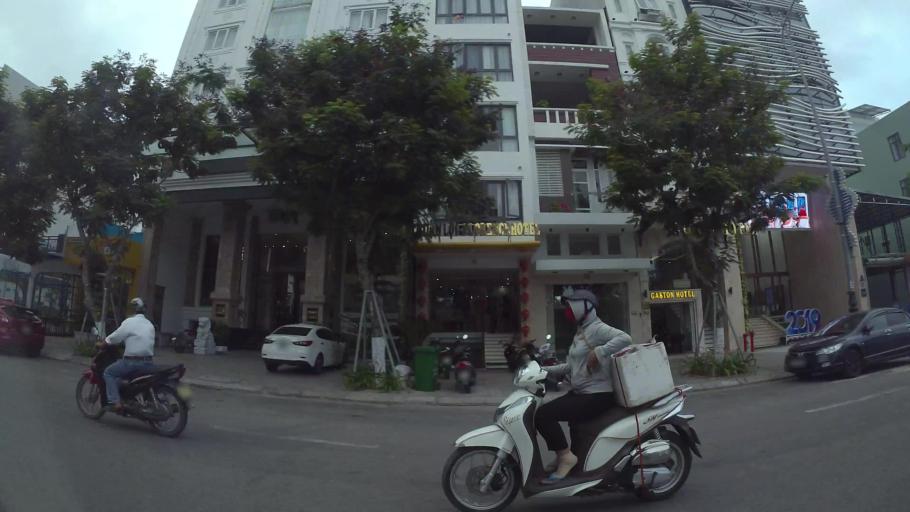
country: VN
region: Da Nang
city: Son Tra
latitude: 16.0621
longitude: 108.2377
